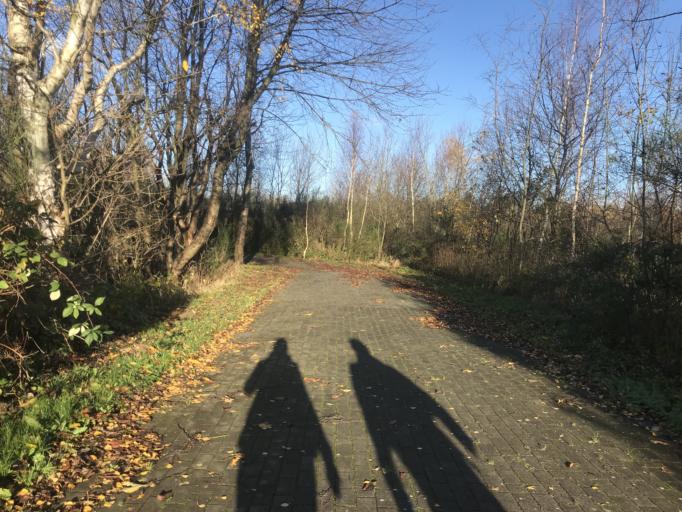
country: PL
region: Pomeranian Voivodeship
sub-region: Powiat pucki
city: Chlapowo
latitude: 54.8081
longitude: 18.3669
